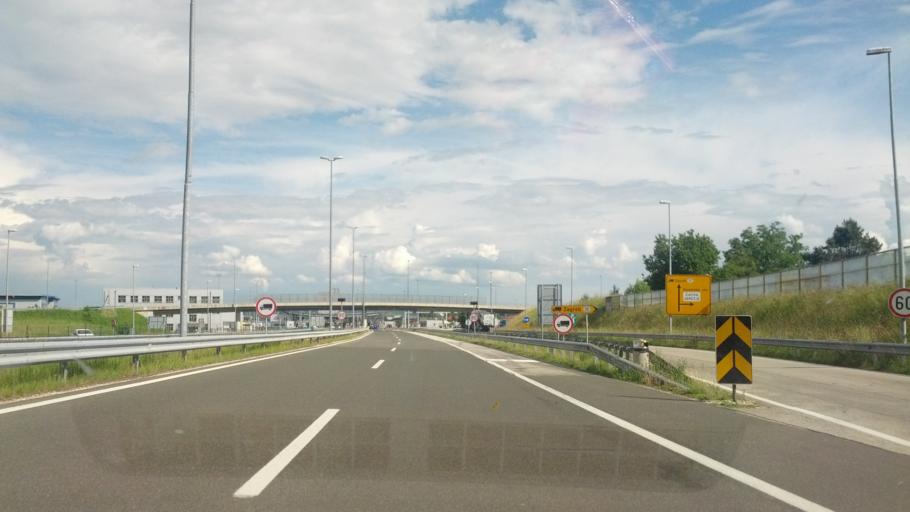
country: HR
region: Zagrebacka
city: Bregana
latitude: 45.8504
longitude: 15.6889
